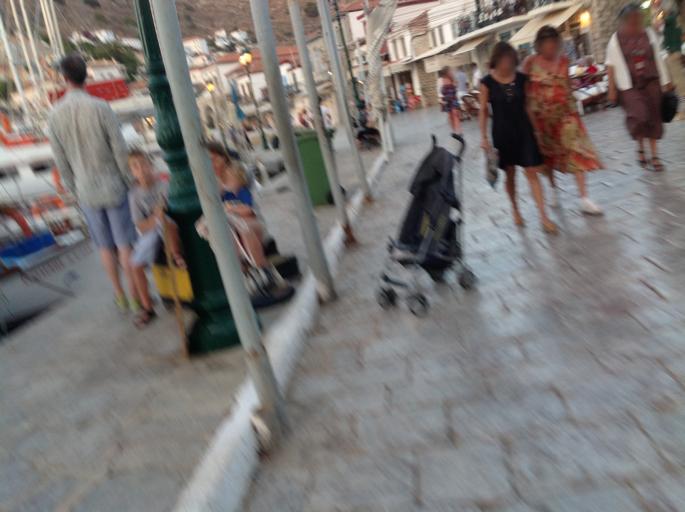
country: GR
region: Attica
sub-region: Nomos Piraios
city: Ydra
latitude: 37.3498
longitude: 23.4654
